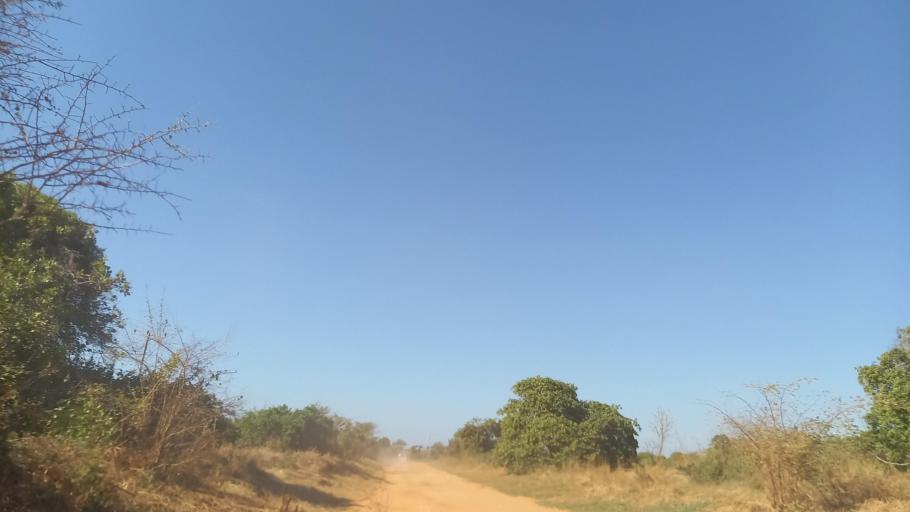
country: MZ
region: Cabo Delgado
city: Pemba
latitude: -13.1583
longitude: 40.5586
